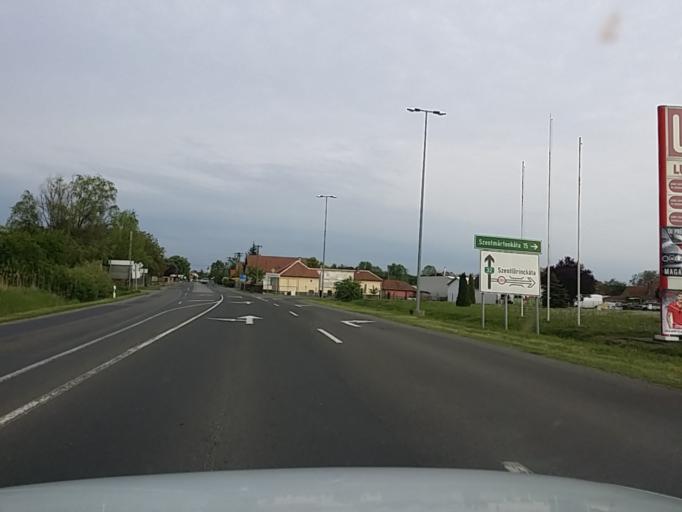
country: HU
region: Pest
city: Szentlorinckata
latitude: 47.5595
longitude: 19.7851
